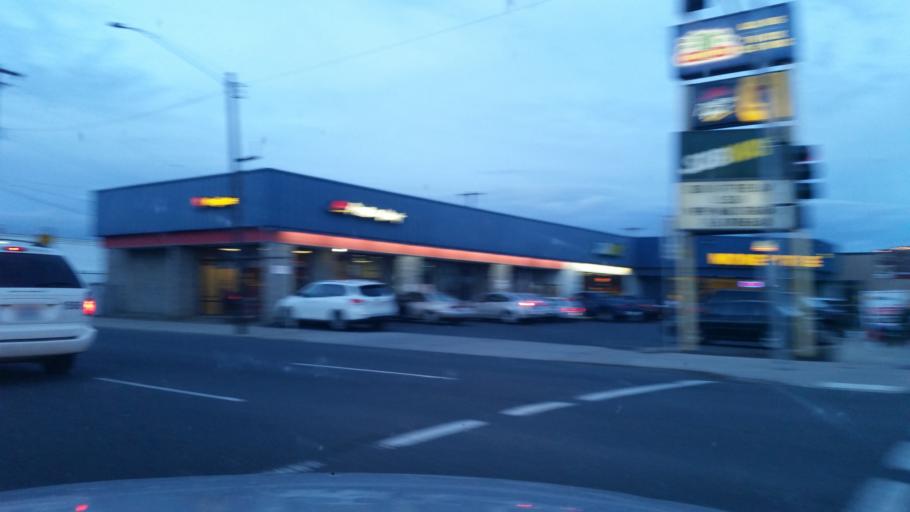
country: US
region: Washington
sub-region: Spokane County
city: Spokane
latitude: 47.6536
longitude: -117.4342
